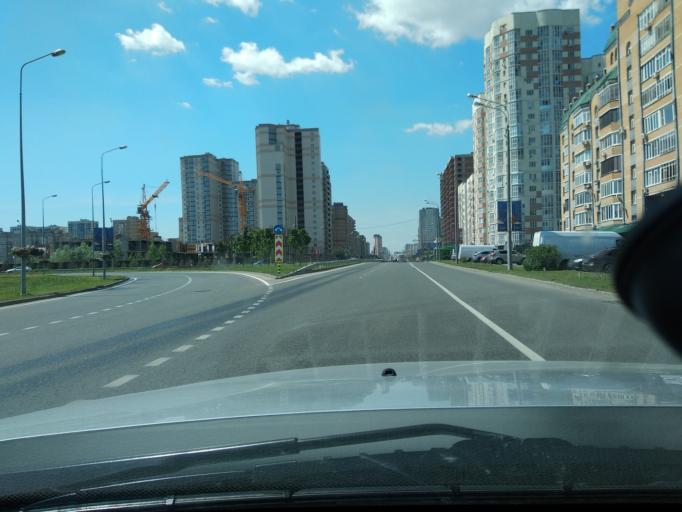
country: RU
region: Tatarstan
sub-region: Gorod Kazan'
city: Kazan
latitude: 55.8195
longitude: 49.1492
